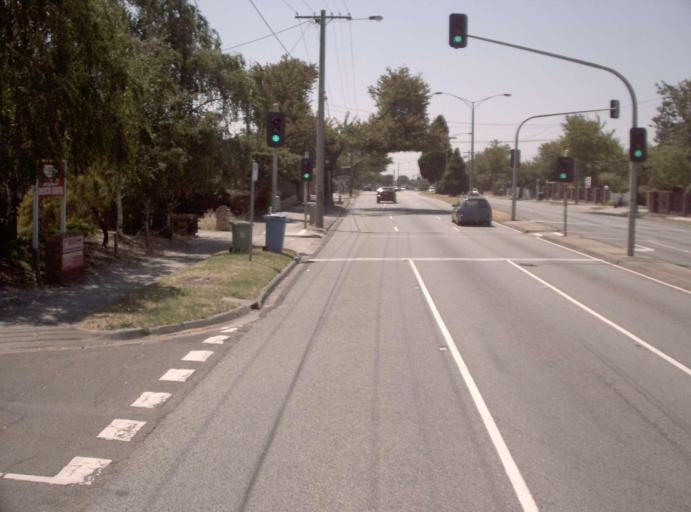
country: AU
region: Victoria
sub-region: Greater Dandenong
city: Springvale South
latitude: -37.9594
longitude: 145.1508
